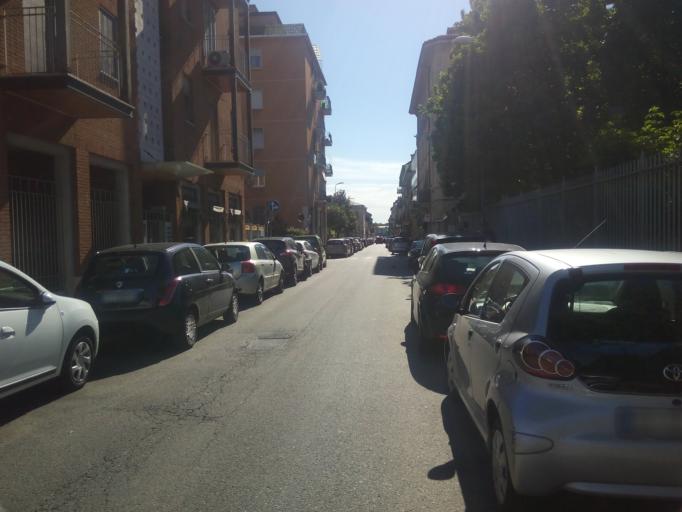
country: IT
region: Lombardy
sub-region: Citta metropolitana di Milano
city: Novate Milanese
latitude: 45.5040
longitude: 9.1664
